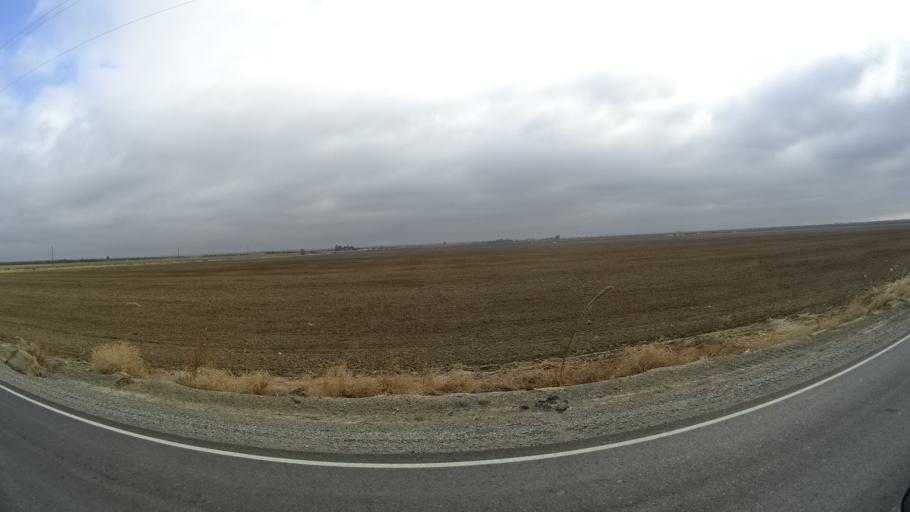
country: US
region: California
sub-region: Yolo County
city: Esparto
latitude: 38.7505
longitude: -122.0445
